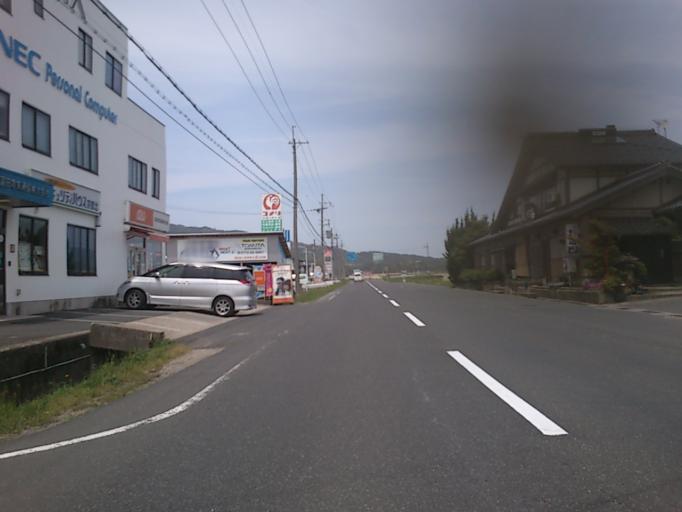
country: JP
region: Kyoto
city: Miyazu
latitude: 35.6678
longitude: 135.0864
